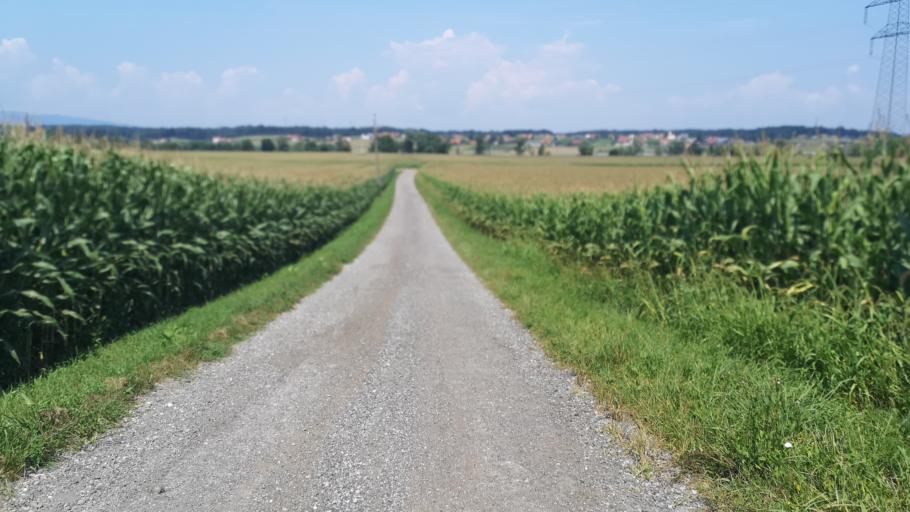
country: AT
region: Styria
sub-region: Politischer Bezirk Deutschlandsberg
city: Wettmannstatten
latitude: 46.8266
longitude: 15.3696
